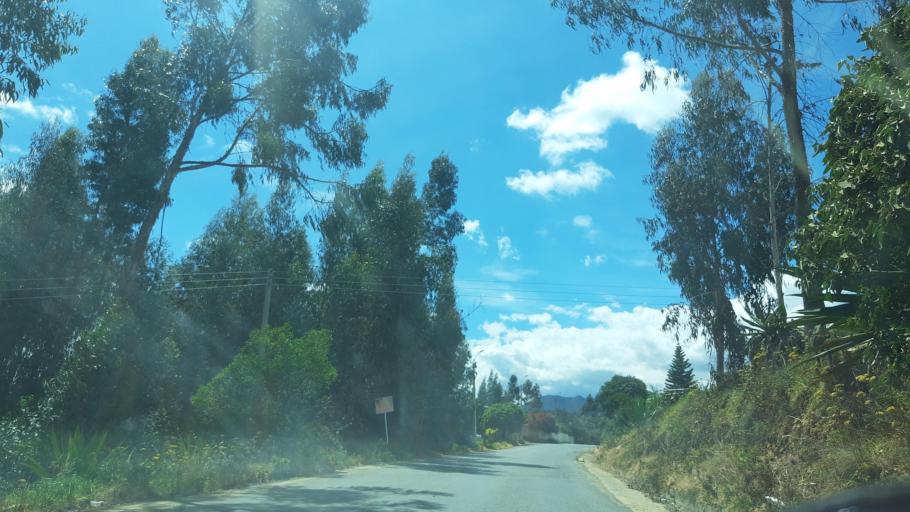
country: CO
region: Boyaca
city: Cucaita
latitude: 5.5393
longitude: -73.4979
